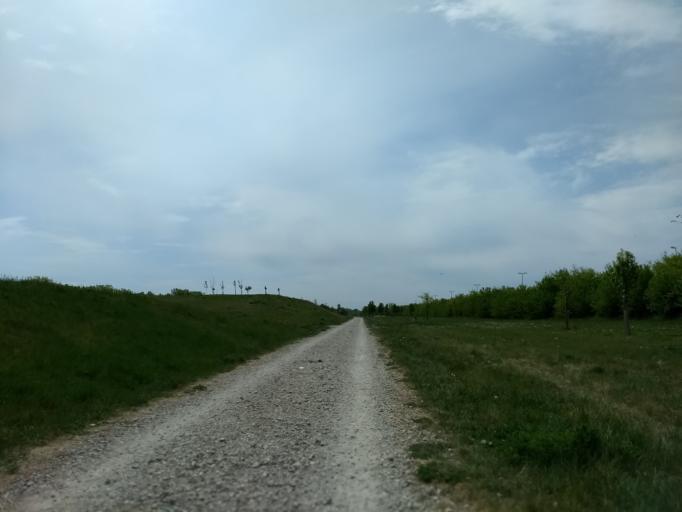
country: AT
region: Lower Austria
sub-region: Politischer Bezirk Ganserndorf
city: Gross-Enzersdorf
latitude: 48.2284
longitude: 16.5153
